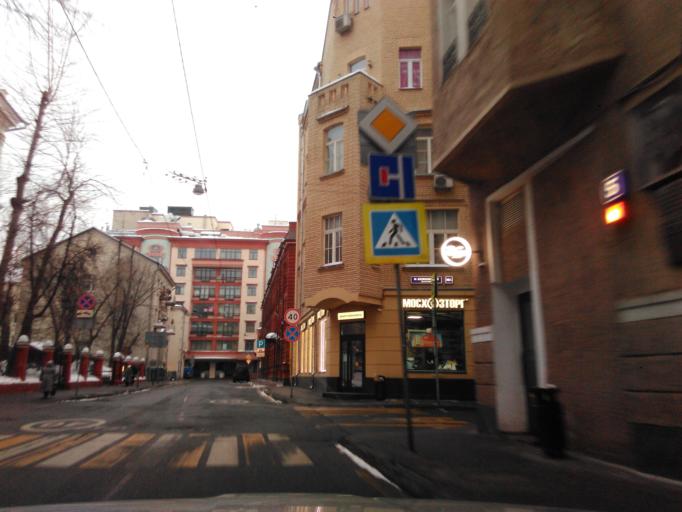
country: RU
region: Moscow
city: Moscow
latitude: 55.7651
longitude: 37.5978
